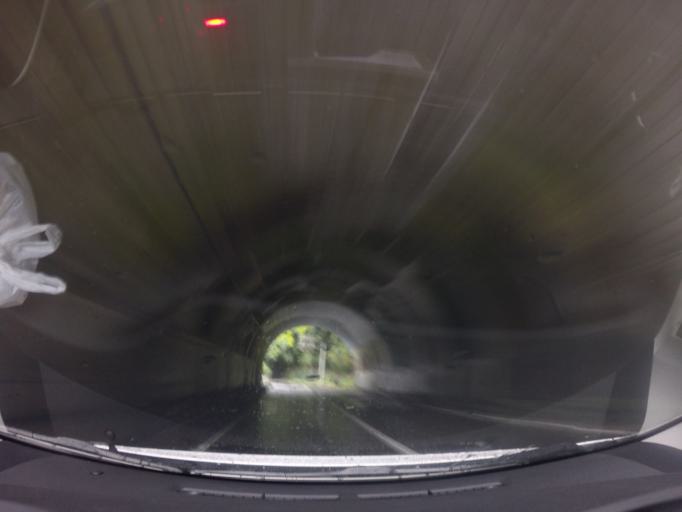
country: JP
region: Wakayama
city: Koya
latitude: 34.0621
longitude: 135.7456
